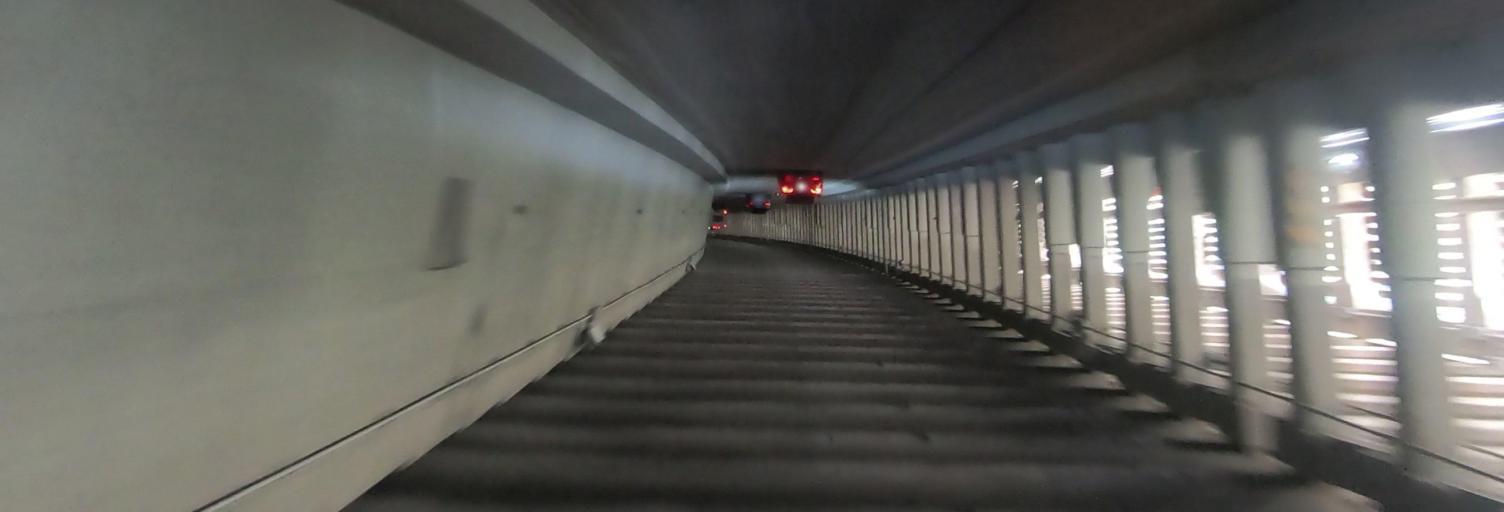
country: CA
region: British Columbia
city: Golden
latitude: 51.3292
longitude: -117.4613
